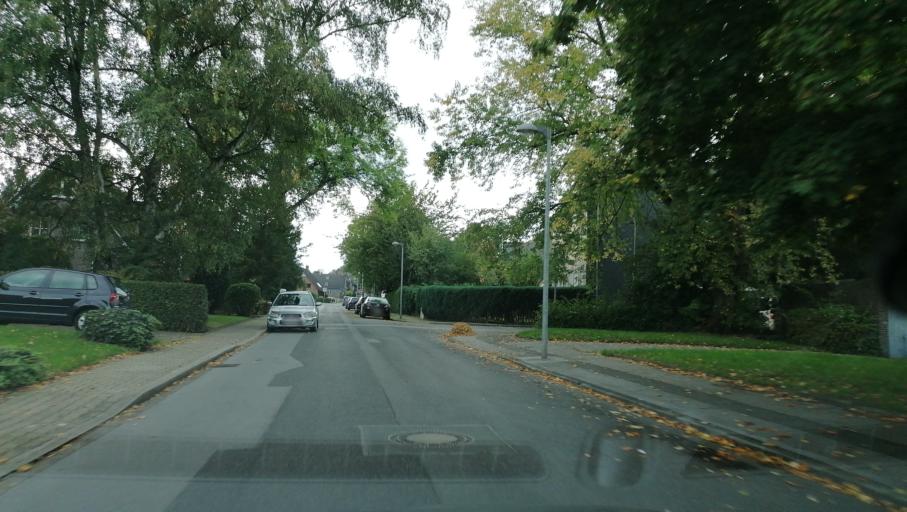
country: DE
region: North Rhine-Westphalia
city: Herten
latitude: 51.5761
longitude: 7.1056
